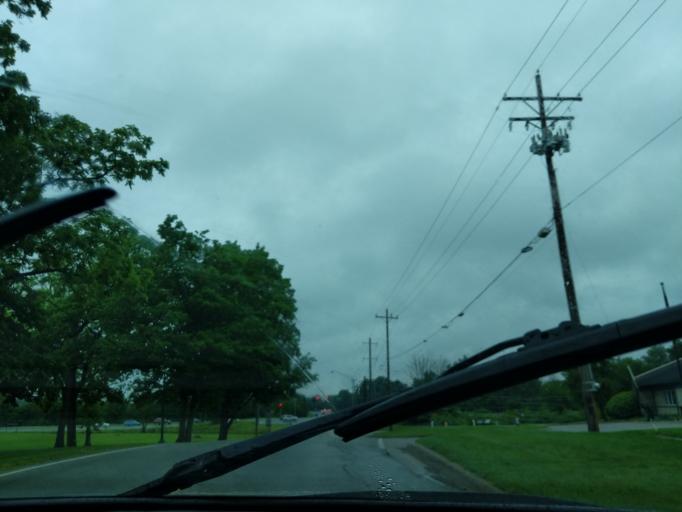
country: US
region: Indiana
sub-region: Hamilton County
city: Noblesville
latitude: 40.0657
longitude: -85.9884
